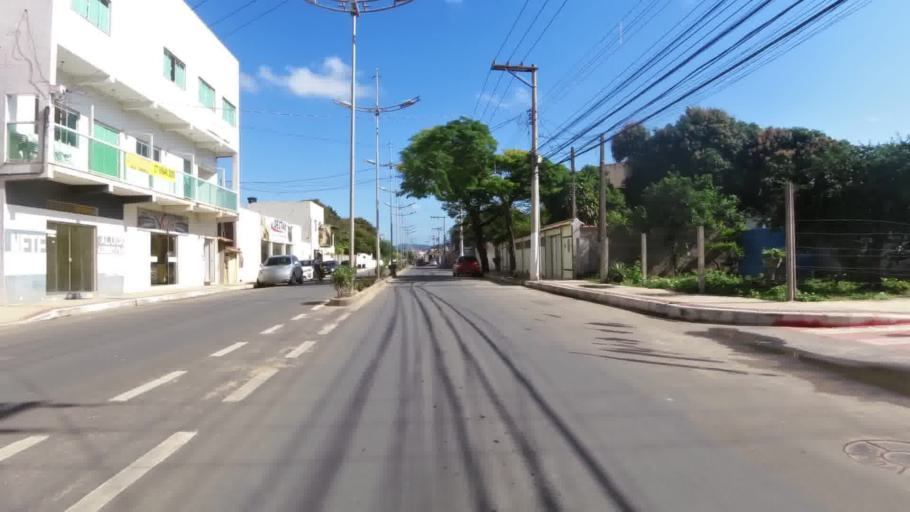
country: BR
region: Espirito Santo
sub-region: Piuma
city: Piuma
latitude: -20.8105
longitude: -40.6365
